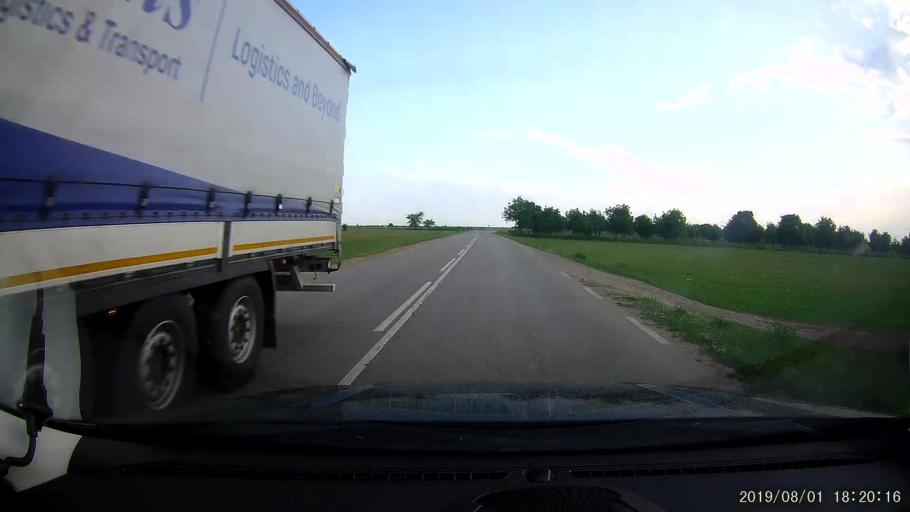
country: BG
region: Shumen
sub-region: Obshtina Kaolinovo
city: Kaolinovo
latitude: 43.6747
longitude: 27.0898
